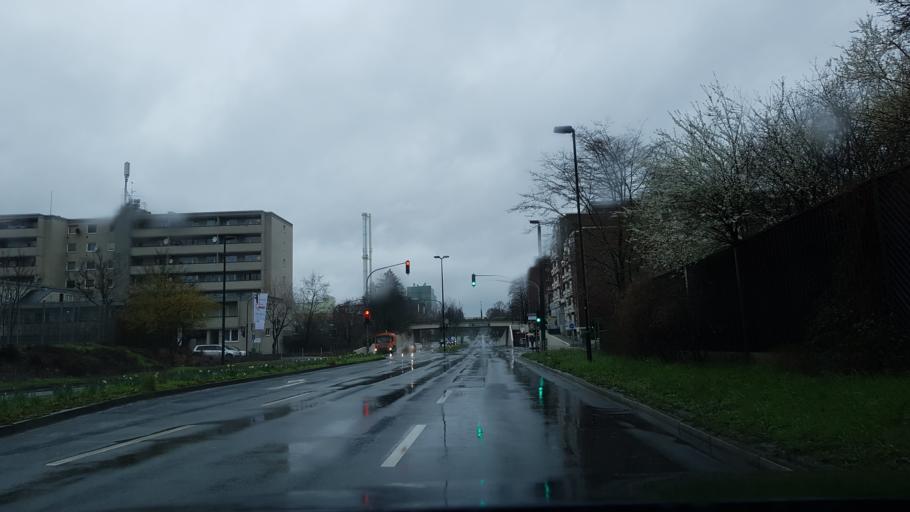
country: DE
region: North Rhine-Westphalia
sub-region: Regierungsbezirk Dusseldorf
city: Hilden
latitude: 51.1434
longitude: 6.9008
